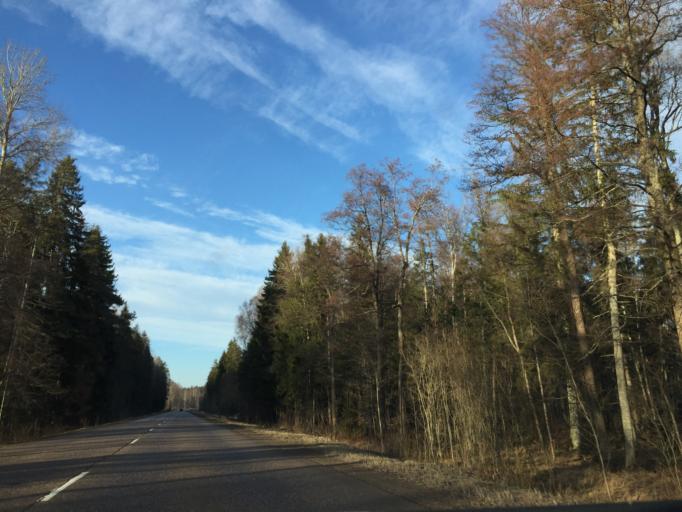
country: LV
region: Kekava
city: Balozi
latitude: 56.7449
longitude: 24.1079
